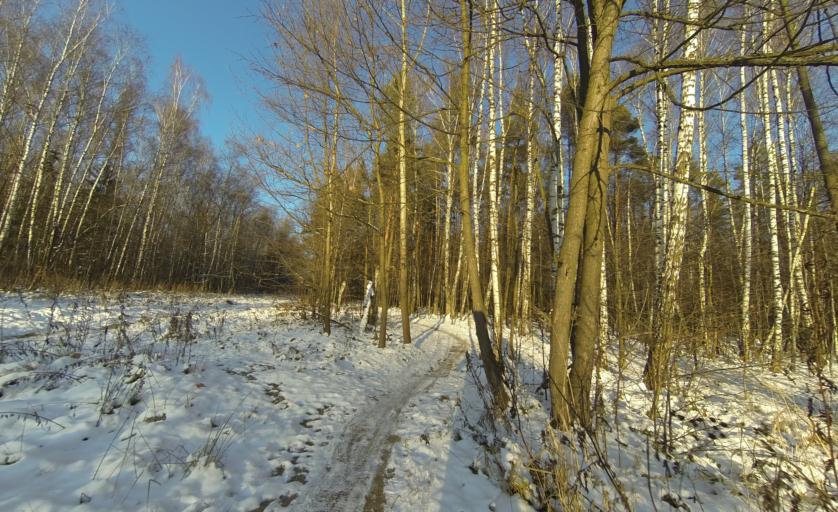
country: RU
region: Moscow
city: Babushkin
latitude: 55.8435
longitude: 37.7627
